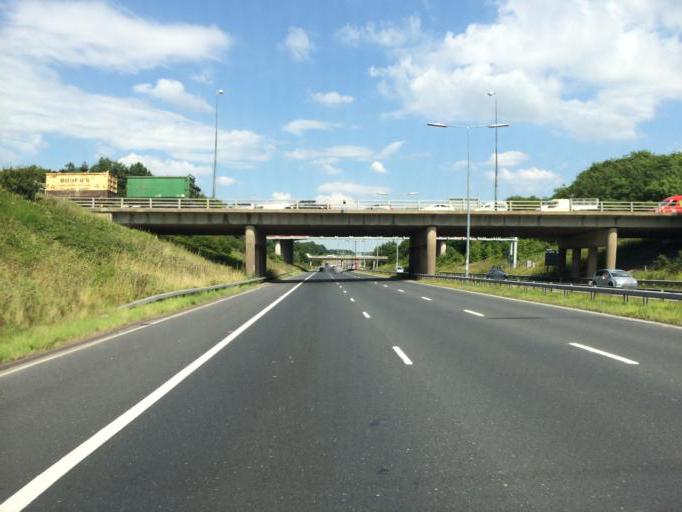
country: GB
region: England
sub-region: Knowsley
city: Huyton
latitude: 53.3975
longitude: -2.8114
